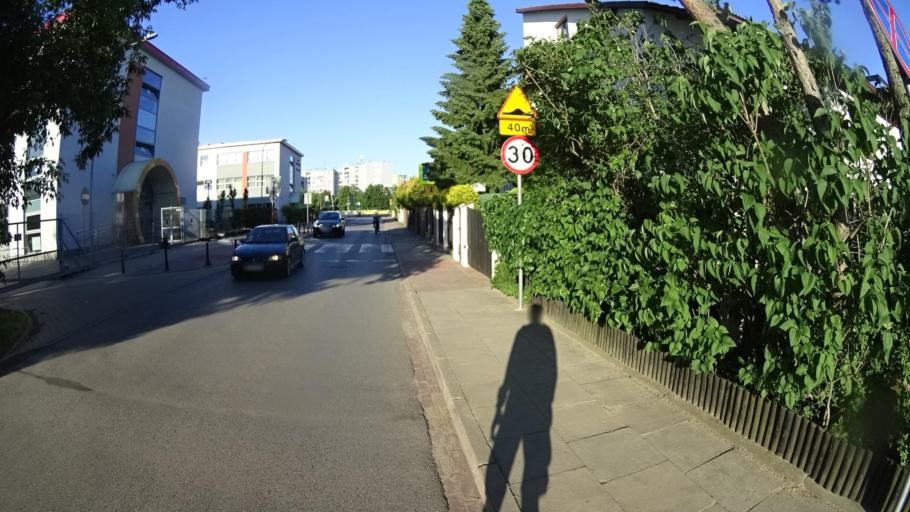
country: PL
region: Masovian Voivodeship
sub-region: Warszawa
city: Bemowo
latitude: 52.2593
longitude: 20.9155
